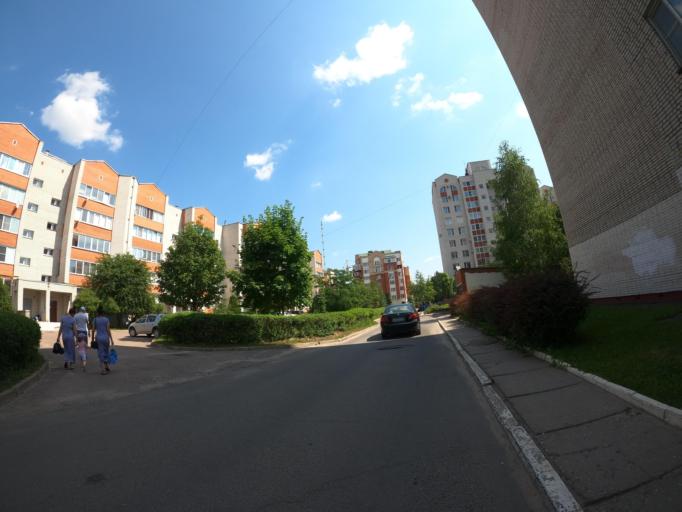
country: RU
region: Kaluga
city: Obninsk
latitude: 55.1160
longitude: 36.5855
